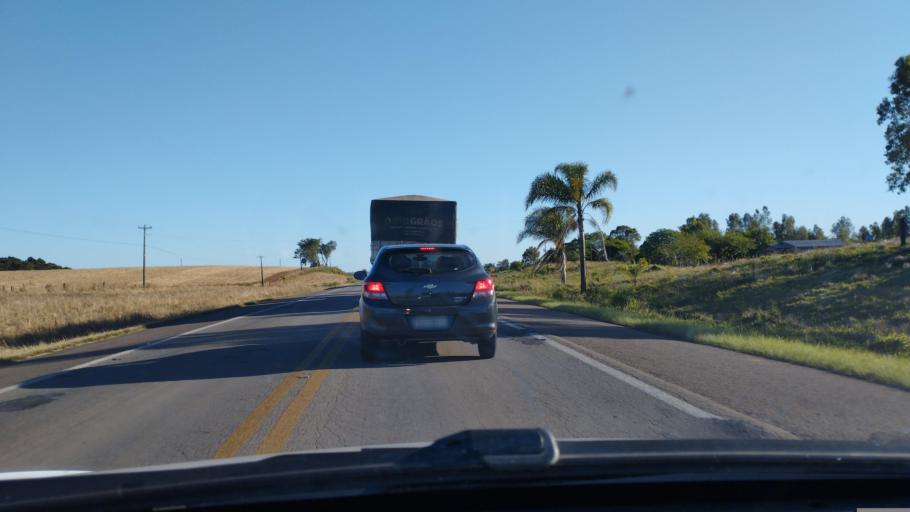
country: BR
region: Rio Grande do Sul
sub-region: Julio De Castilhos
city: Julio de Castilhos
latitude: -29.3791
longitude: -53.6705
